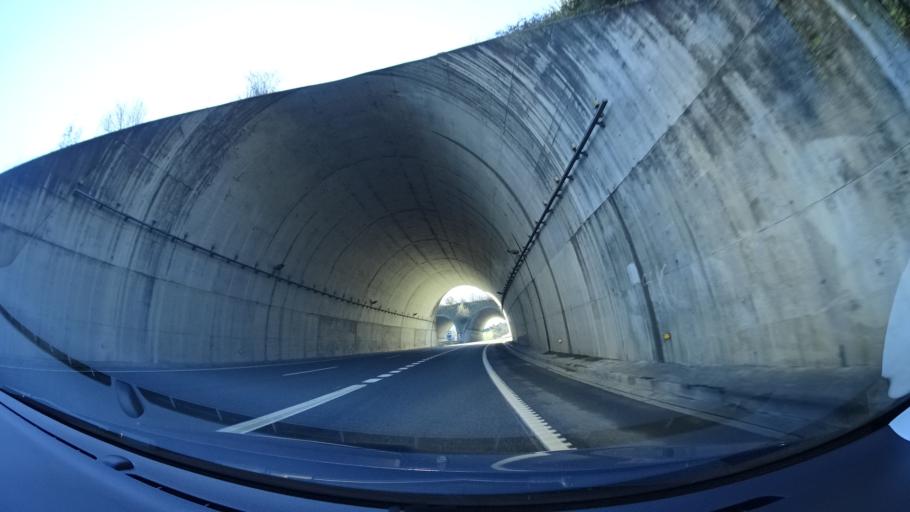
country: ES
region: Basque Country
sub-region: Provincia de Guipuzcoa
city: Astigarraga
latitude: 43.2806
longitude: -1.9593
